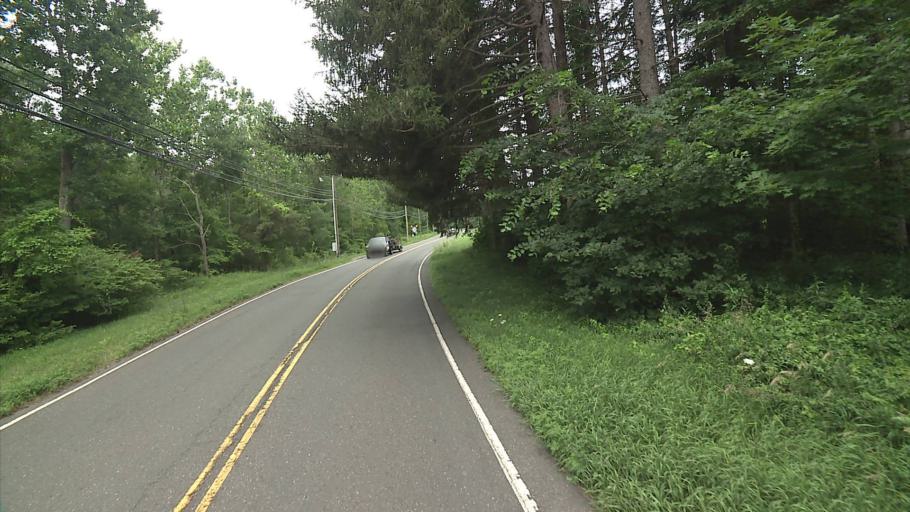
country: US
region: Connecticut
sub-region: Litchfield County
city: New Milford
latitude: 41.5490
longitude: -73.3363
